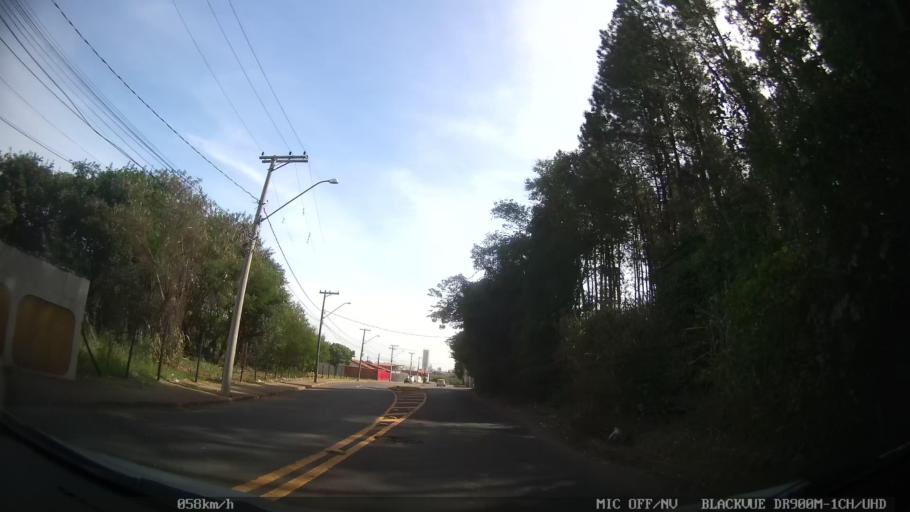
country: BR
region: Sao Paulo
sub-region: Piracicaba
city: Piracicaba
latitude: -22.7562
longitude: -47.6066
